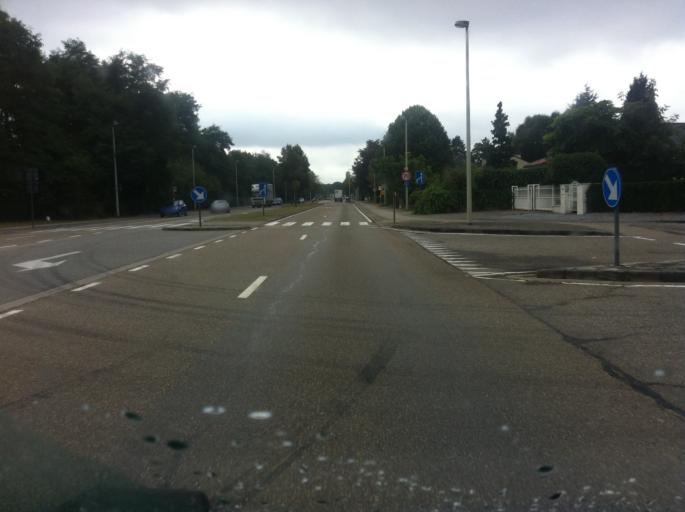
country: BE
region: Flanders
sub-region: Provincie Limburg
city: Lanaken
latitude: 50.9060
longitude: 5.6796
